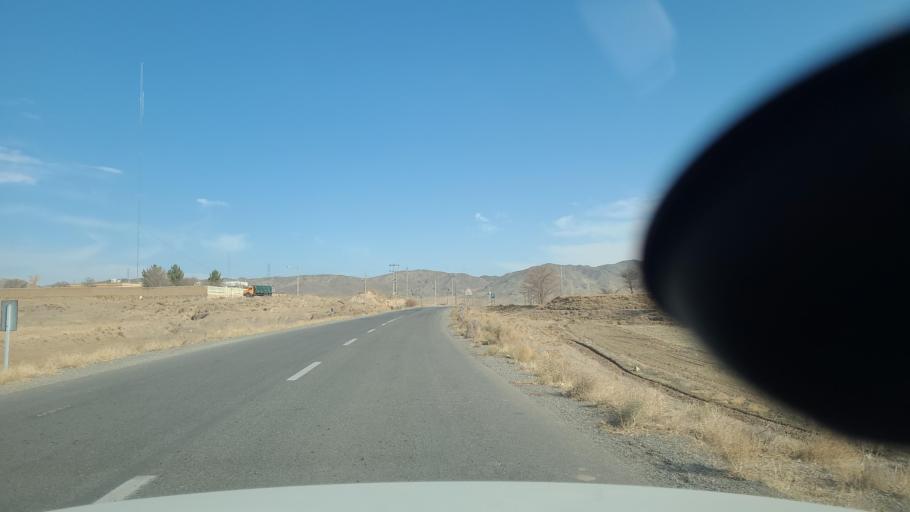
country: IR
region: Razavi Khorasan
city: Fariman
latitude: 35.5964
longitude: 59.6961
